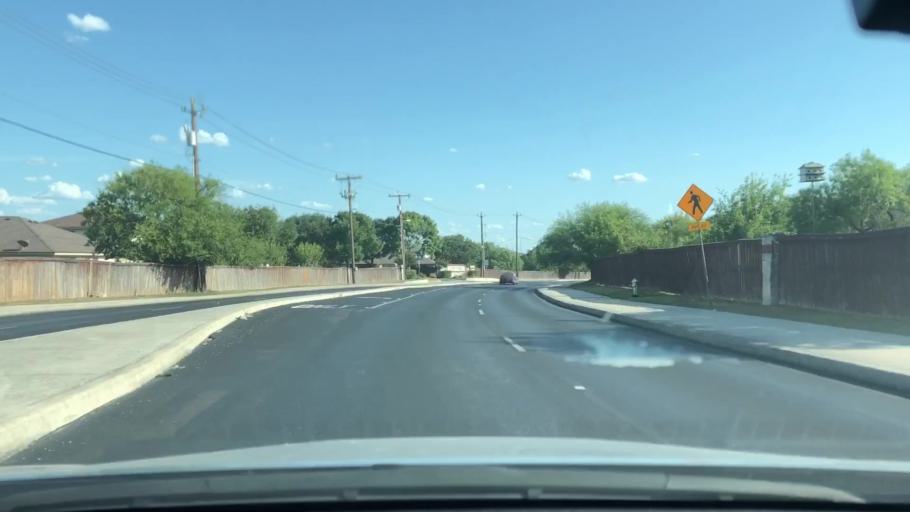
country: US
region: Texas
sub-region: Bexar County
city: Kirby
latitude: 29.4751
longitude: -98.3458
